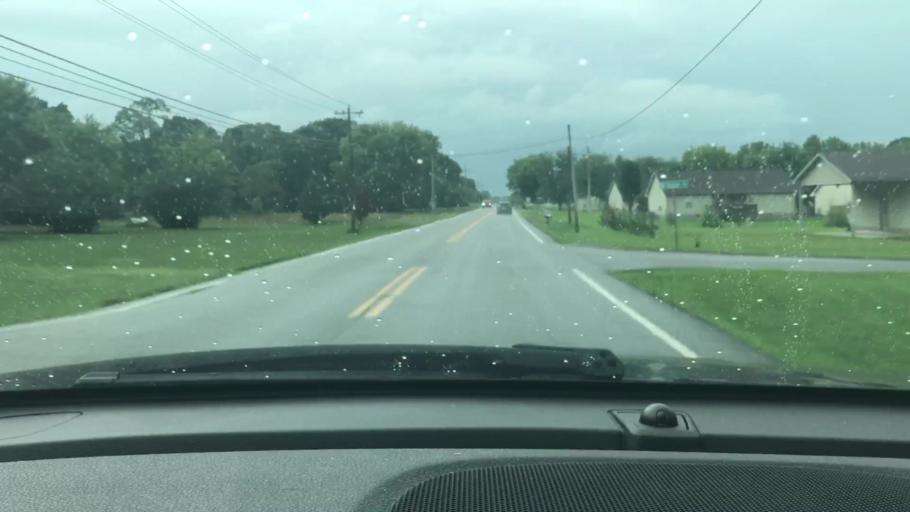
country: US
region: Tennessee
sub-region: Sumner County
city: Millersville
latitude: 36.4081
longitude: -86.6973
